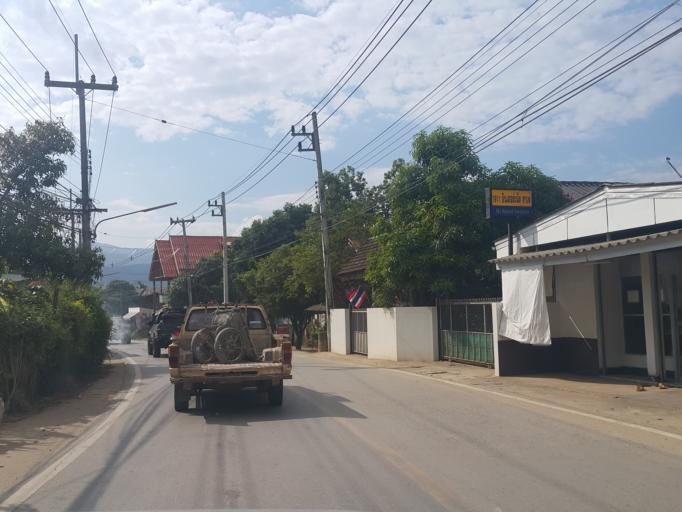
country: TH
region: Chiang Mai
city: Mae Chaem
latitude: 18.5000
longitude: 98.3677
